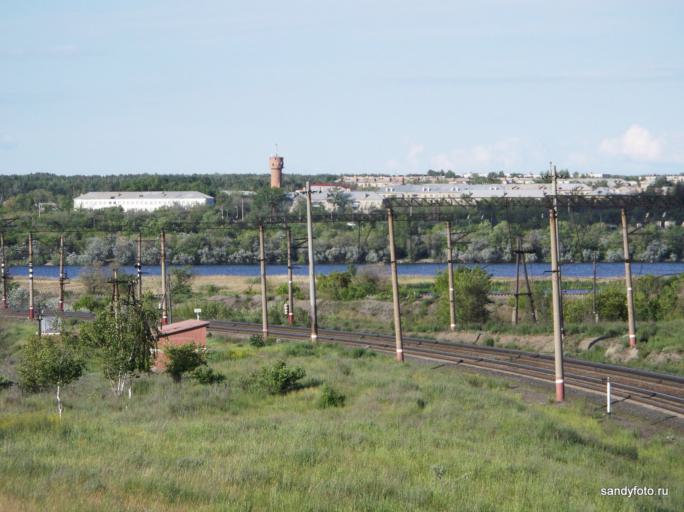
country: RU
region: Chelyabinsk
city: Troitsk
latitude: 54.0373
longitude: 61.6052
